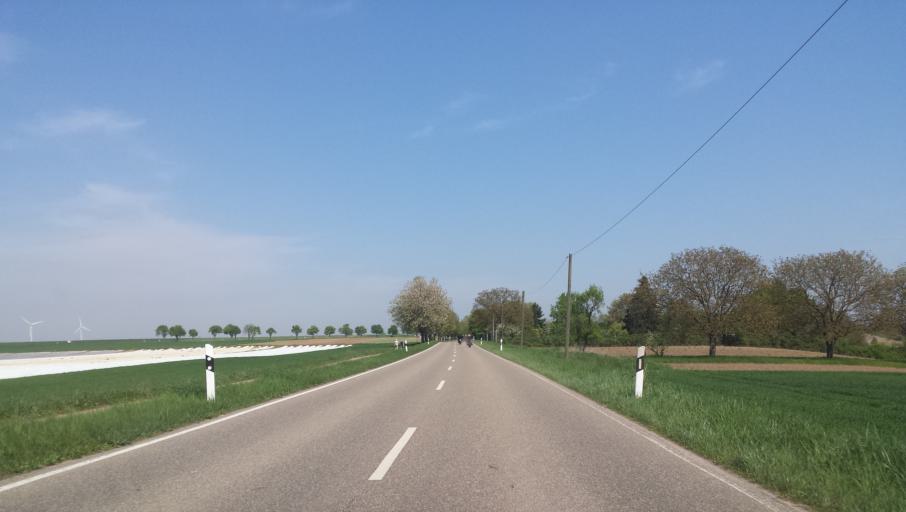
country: DE
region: Rheinland-Pfalz
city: Lingenfeld
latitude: 49.2631
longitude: 8.3722
